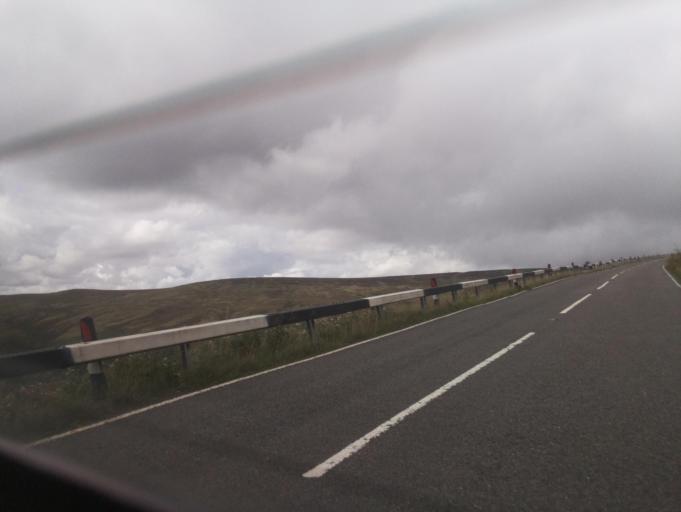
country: GB
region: England
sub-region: Kirklees
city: Meltham
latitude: 53.5247
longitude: -1.8534
